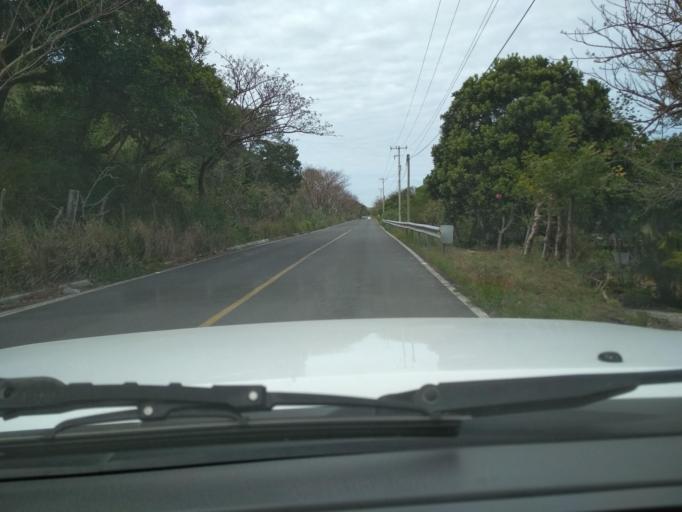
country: MX
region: Veracruz
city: Anton Lizardo
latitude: 19.0389
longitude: -95.9854
